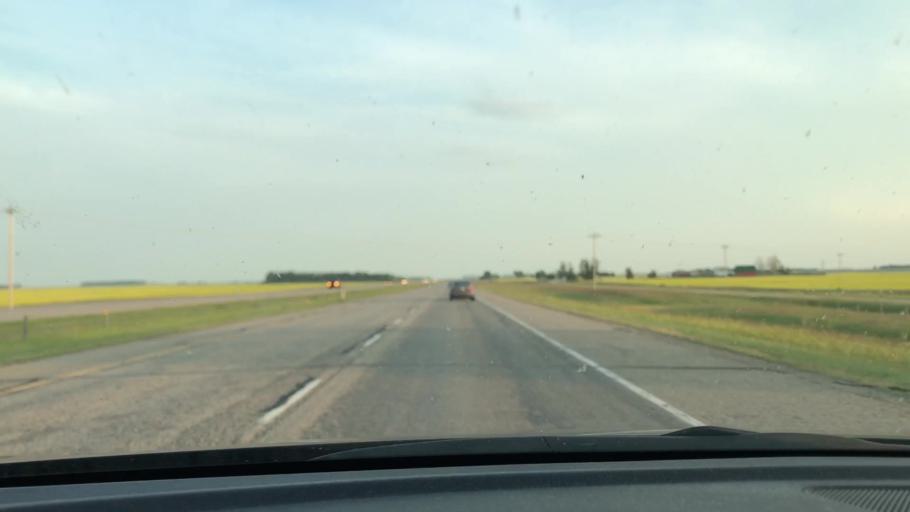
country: CA
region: Alberta
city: Olds
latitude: 51.8472
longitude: -114.0256
